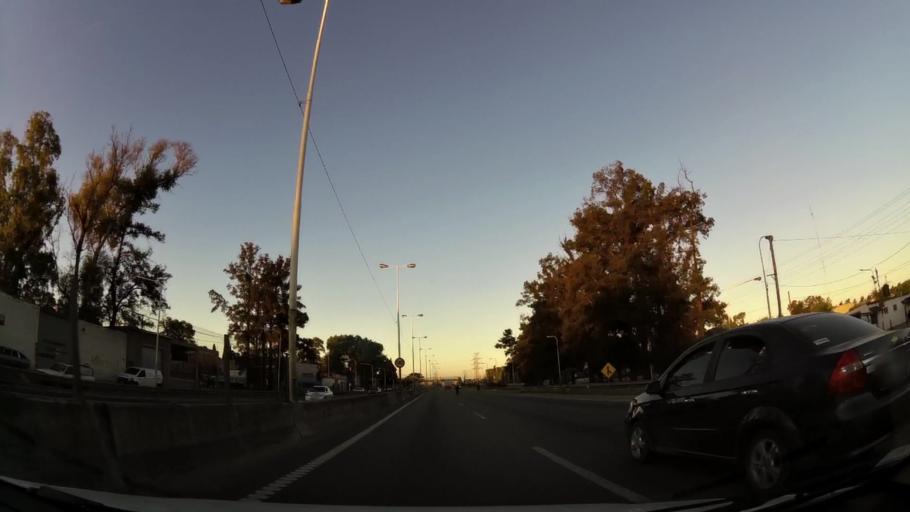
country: AR
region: Buenos Aires
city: Pontevedra
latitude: -34.7854
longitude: -58.6267
